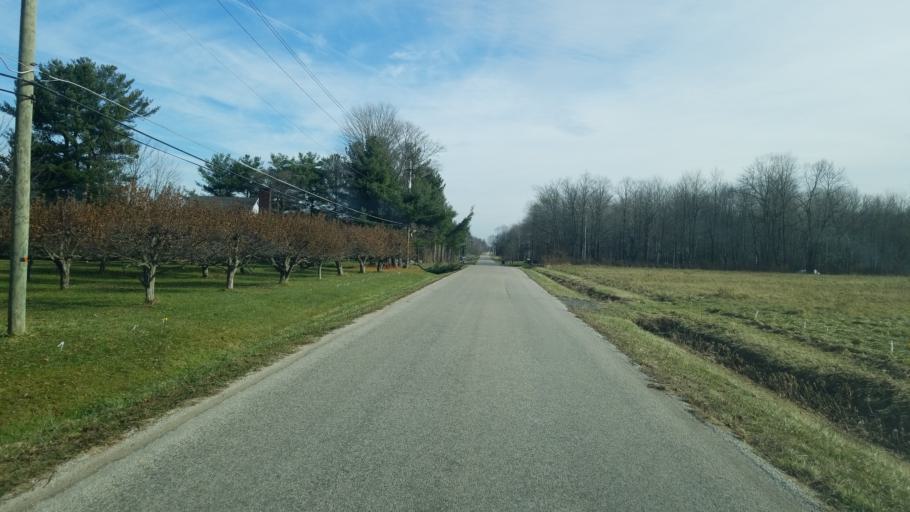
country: US
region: Ohio
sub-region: Ashtabula County
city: Geneva
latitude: 41.6985
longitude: -80.9462
